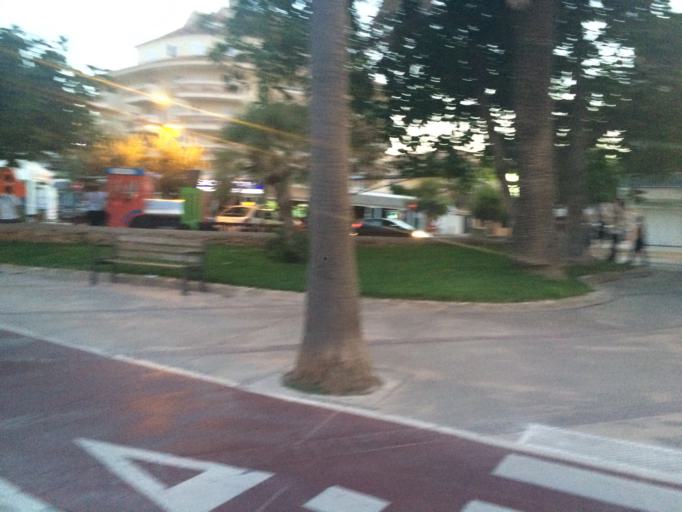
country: ES
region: Balearic Islands
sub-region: Illes Balears
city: Son Servera
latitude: 39.6103
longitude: 3.3899
